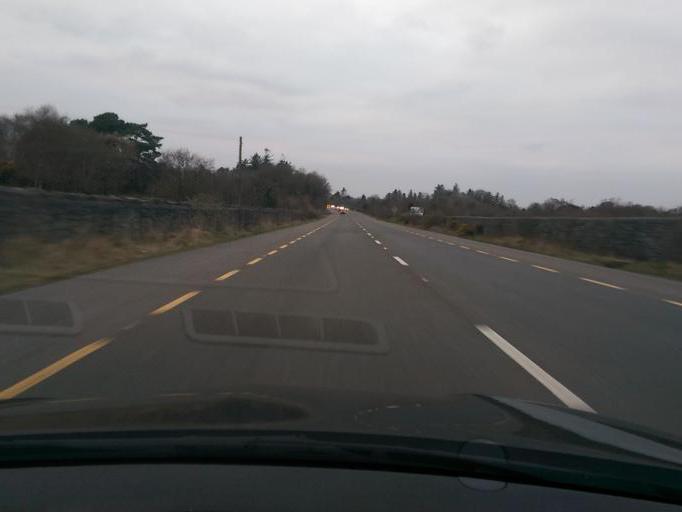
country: IE
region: Connaught
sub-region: County Galway
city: Moycullen
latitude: 53.3175
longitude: -9.1543
